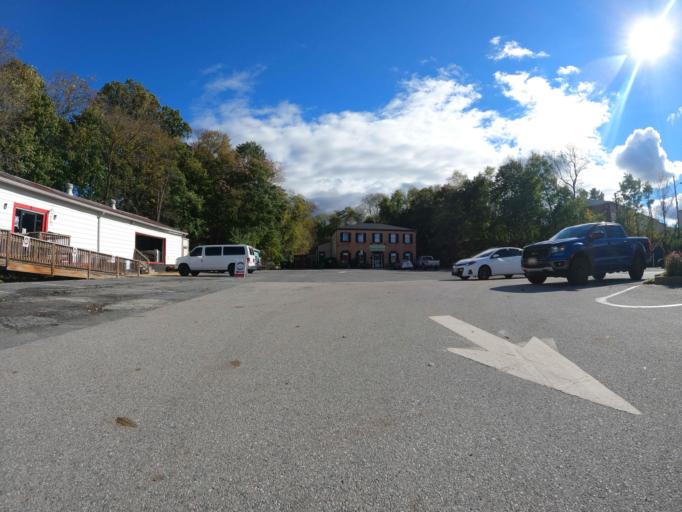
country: US
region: Maryland
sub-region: Carroll County
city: Mount Airy
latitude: 39.3768
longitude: -77.1538
